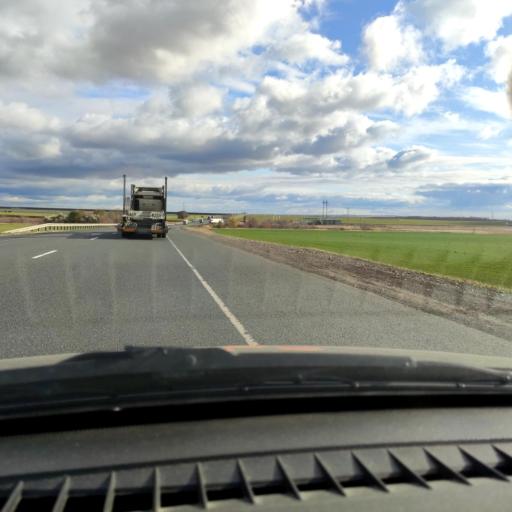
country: RU
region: Samara
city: Varlamovo
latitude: 53.2128
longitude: 48.4055
